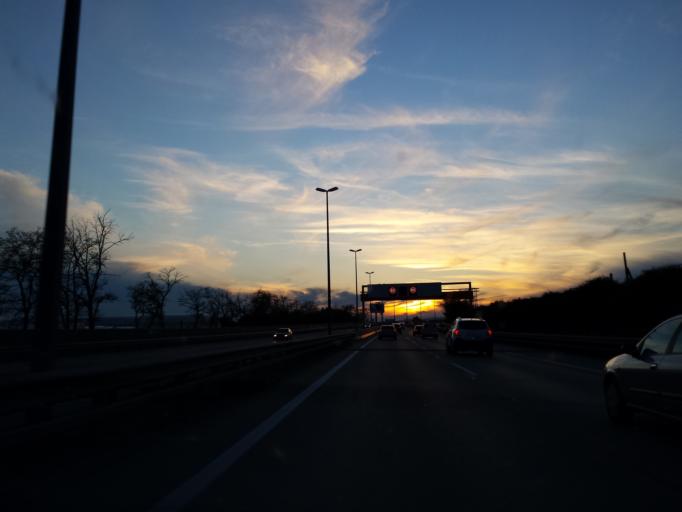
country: AT
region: Lower Austria
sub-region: Politischer Bezirk Wien-Umgebung
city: Schwechat
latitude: 48.1663
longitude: 16.4640
